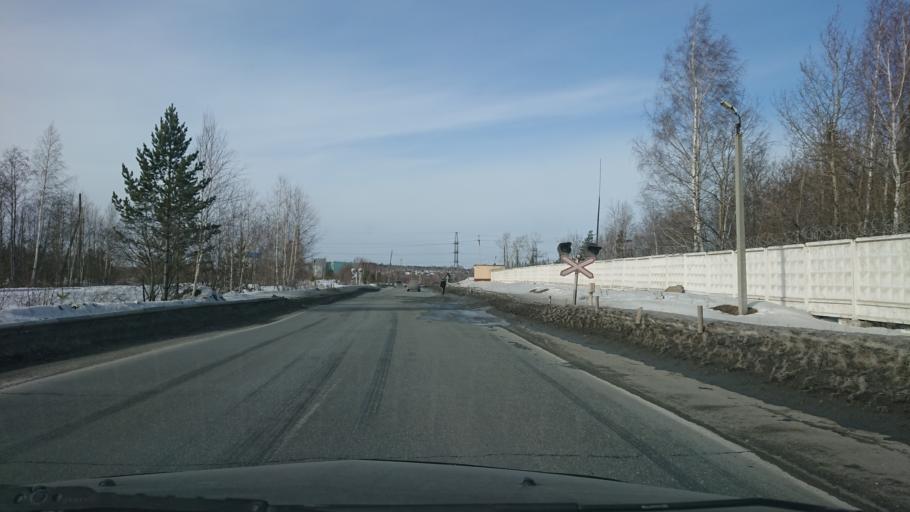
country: RU
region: Sverdlovsk
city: Revda
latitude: 56.8088
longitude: 59.9777
